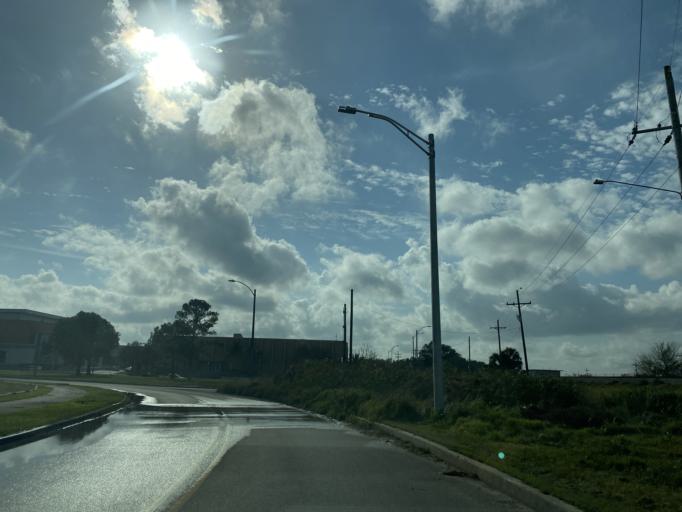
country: US
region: Louisiana
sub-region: Orleans Parish
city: New Orleans
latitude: 30.0286
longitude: -90.0436
